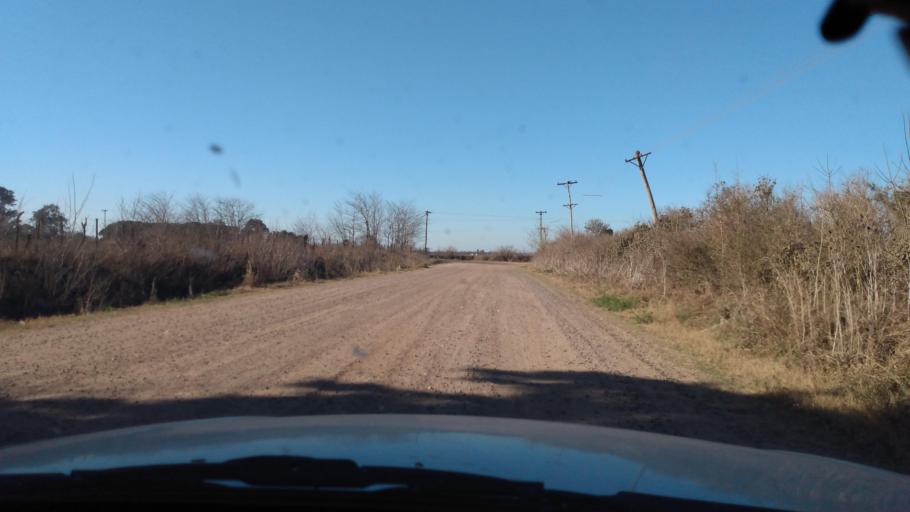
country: AR
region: Buenos Aires
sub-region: Partido de Mercedes
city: Mercedes
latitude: -34.6405
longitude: -59.3730
